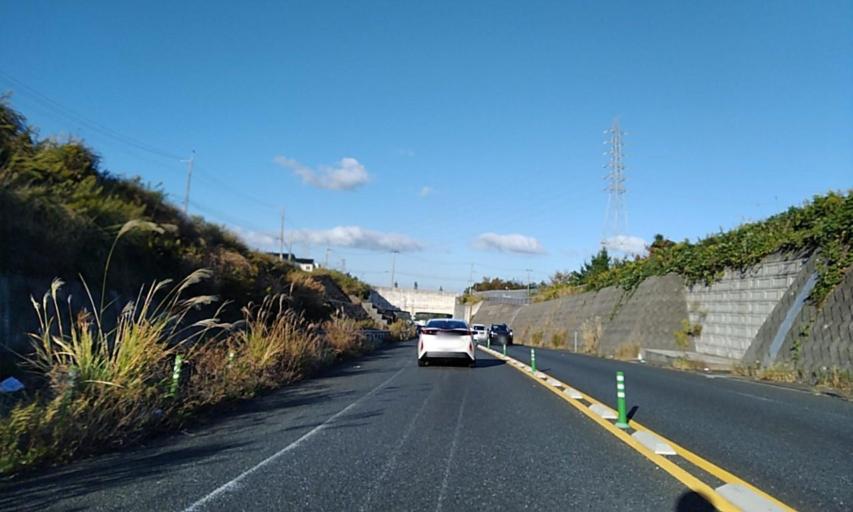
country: JP
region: Wakayama
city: Wakayama-shi
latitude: 34.3258
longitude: 135.1884
